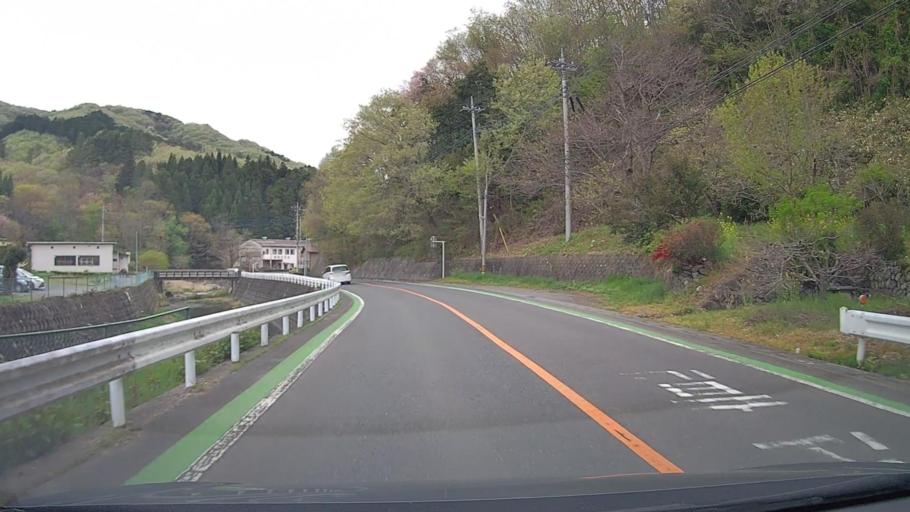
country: JP
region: Saitama
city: Yorii
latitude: 36.0684
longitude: 139.1273
